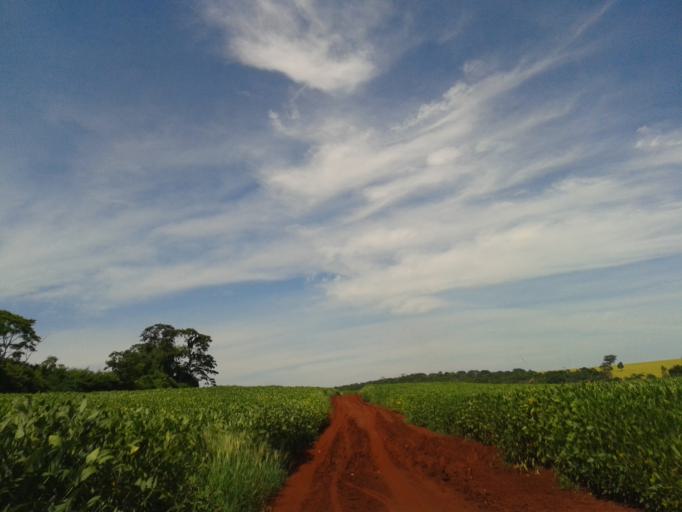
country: BR
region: Minas Gerais
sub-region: Capinopolis
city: Capinopolis
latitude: -18.6612
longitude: -49.7104
